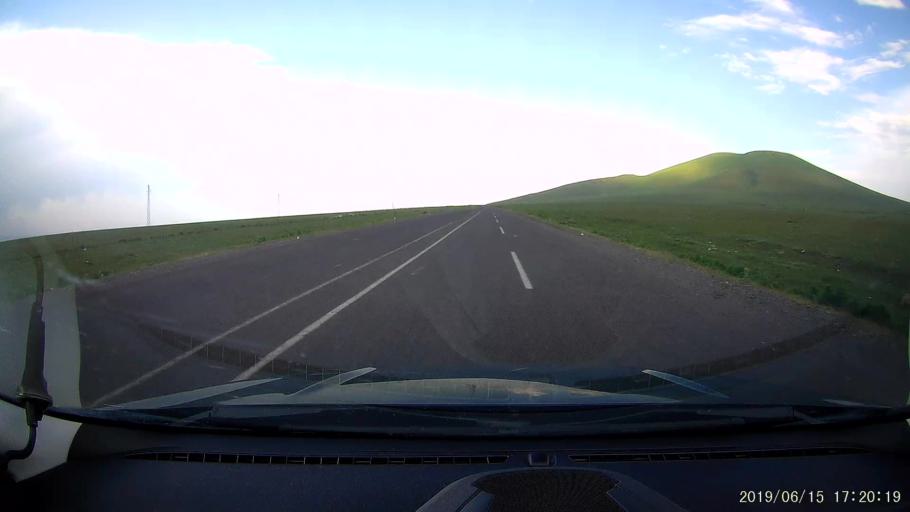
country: TR
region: Kars
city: Kars
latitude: 40.6162
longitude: 43.2985
